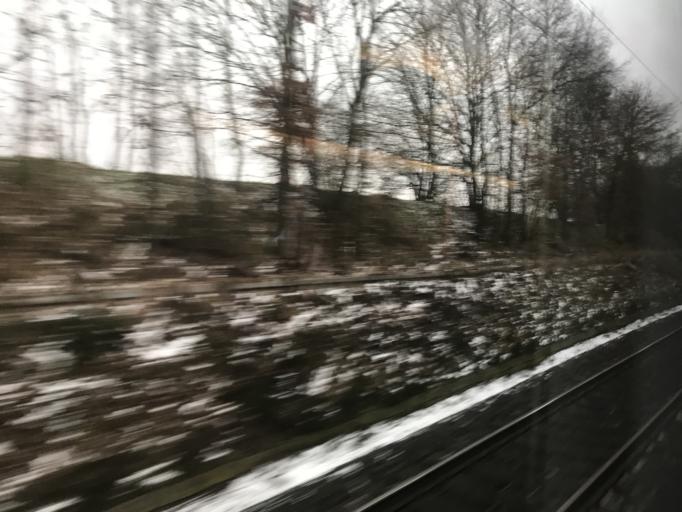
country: DE
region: Hesse
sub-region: Regierungsbezirk Kassel
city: Eichenzell
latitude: 50.4743
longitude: 9.6583
